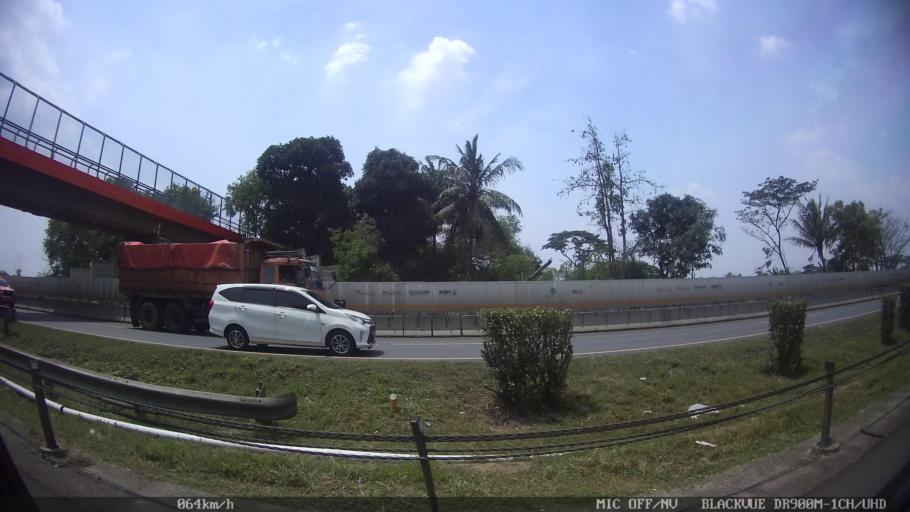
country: ID
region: Banten
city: Serang
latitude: -6.1348
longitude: 106.2113
